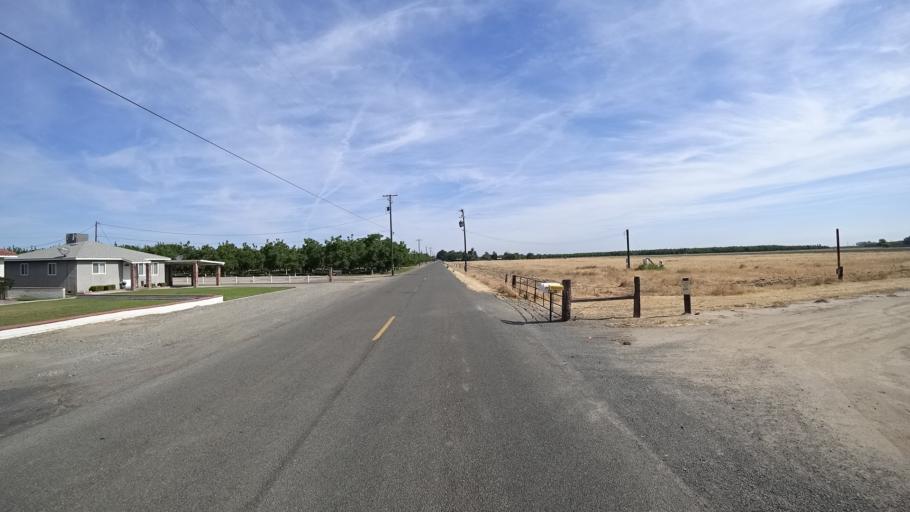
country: US
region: California
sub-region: Kings County
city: Lucerne
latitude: 36.3759
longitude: -119.6100
